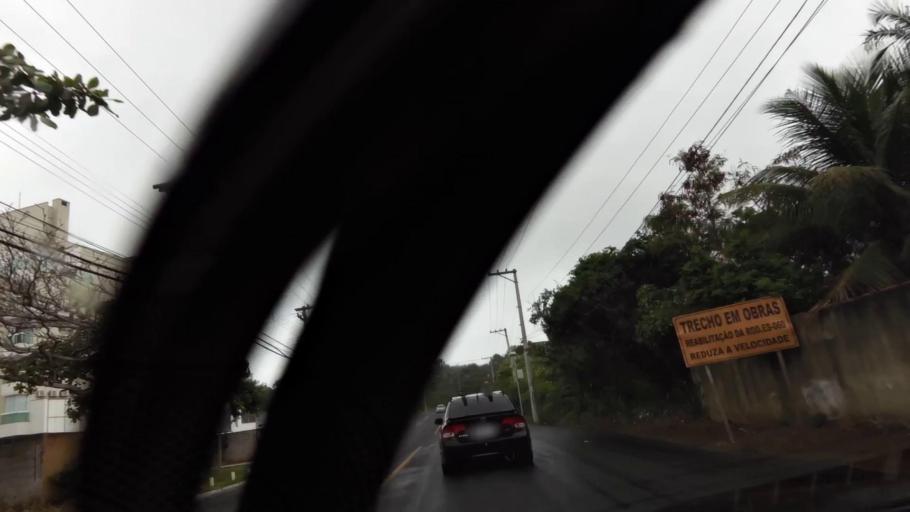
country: BR
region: Espirito Santo
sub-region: Guarapari
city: Guarapari
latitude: -20.7324
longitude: -40.5331
